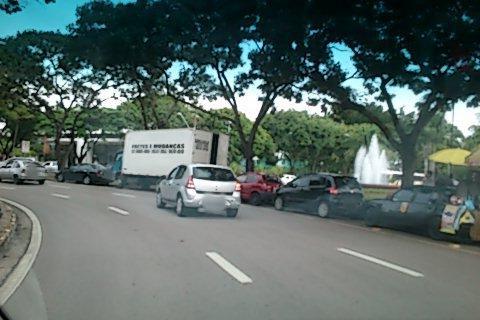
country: BR
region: Sao Paulo
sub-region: Sao Jose Dos Campos
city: Sao Jose dos Campos
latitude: -23.2483
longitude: -45.8857
